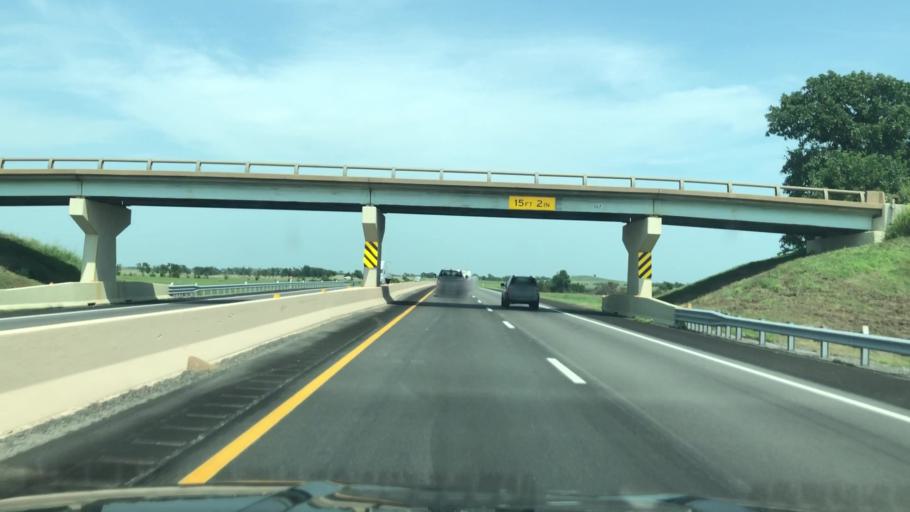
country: US
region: Oklahoma
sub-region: Ottawa County
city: Afton
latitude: 36.6763
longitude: -95.0532
